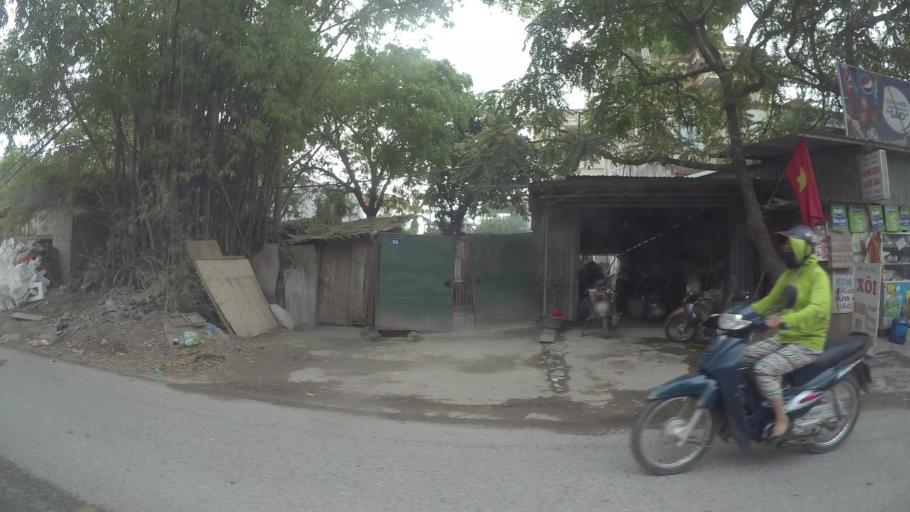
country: VN
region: Ha Noi
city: Cau Dien
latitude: 21.0399
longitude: 105.7380
